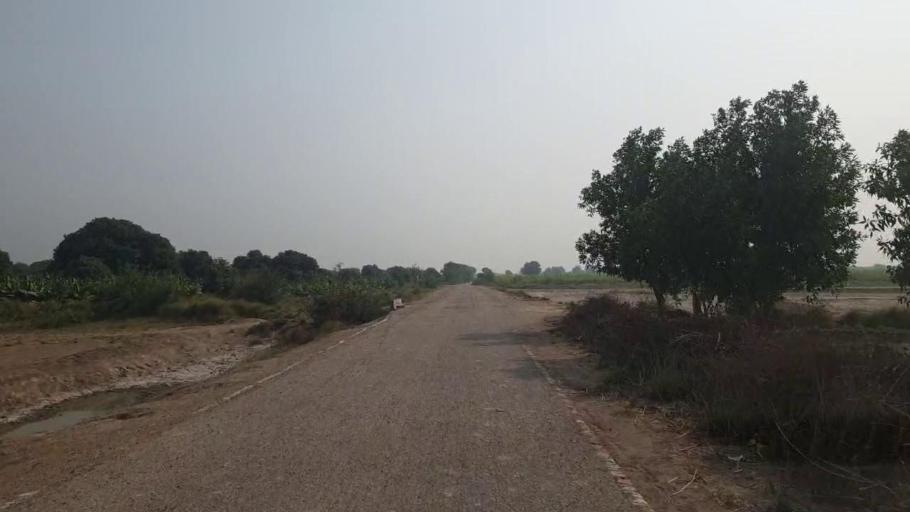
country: PK
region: Sindh
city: Tando Muhammad Khan
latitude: 25.2465
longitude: 68.5610
